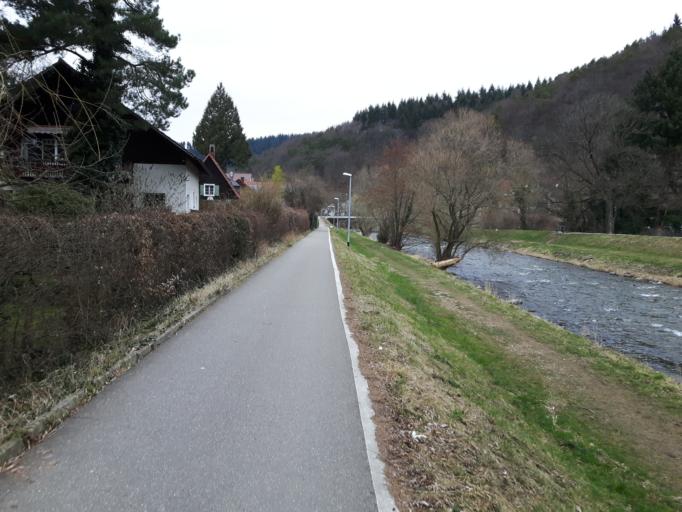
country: DE
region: Baden-Wuerttemberg
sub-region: Freiburg Region
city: Freiburg
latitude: 47.9861
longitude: 7.9000
